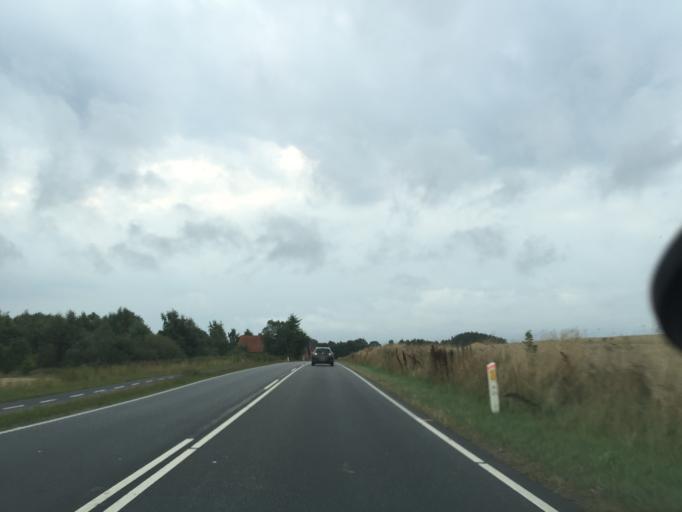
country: DK
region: Central Jutland
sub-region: Skanderborg Kommune
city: Skanderborg
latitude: 56.0938
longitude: 9.8981
